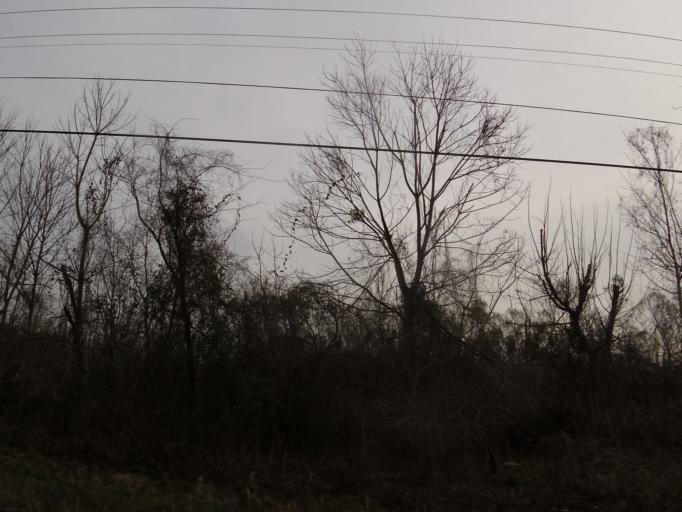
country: US
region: Alabama
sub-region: Montgomery County
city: Montgomery
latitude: 32.3896
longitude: -86.3126
